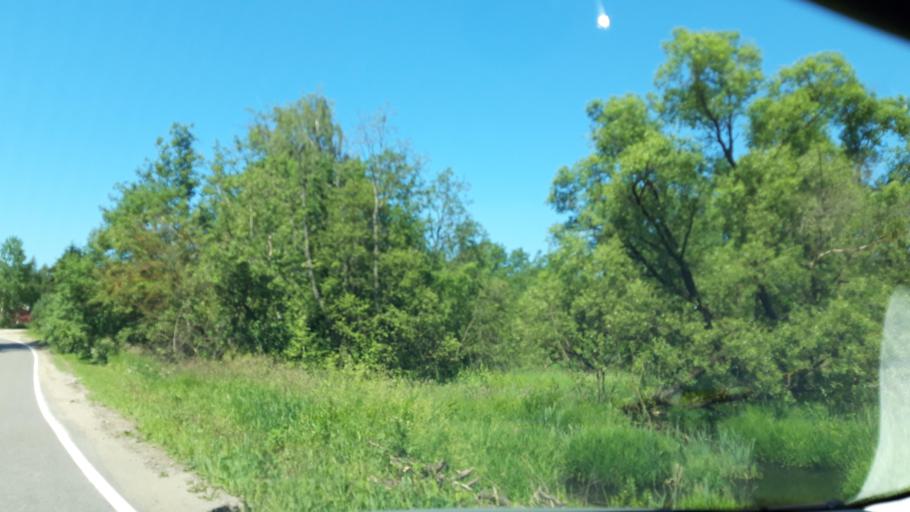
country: RU
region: Moskovskaya
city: Solnechnogorsk
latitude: 56.1653
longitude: 36.9735
